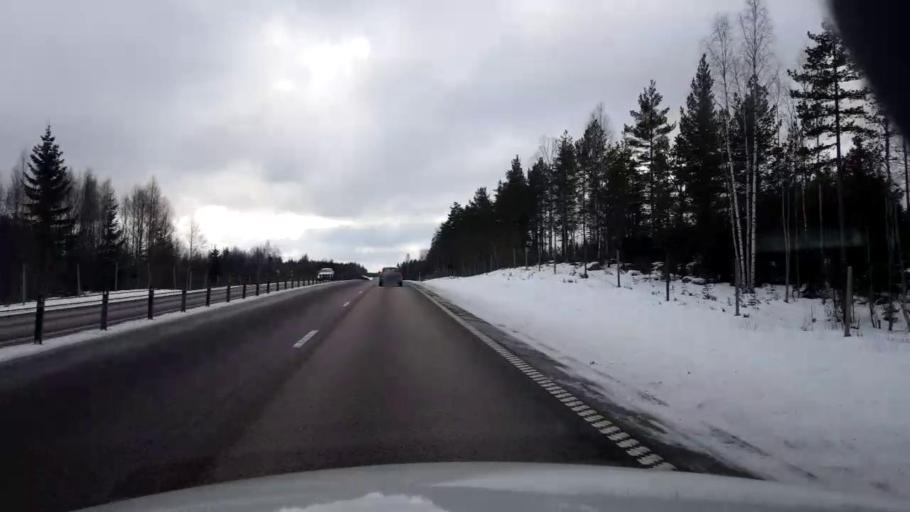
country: SE
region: Gaevleborg
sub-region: Hudiksvalls Kommun
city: Hudiksvall
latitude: 61.8259
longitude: 17.1921
